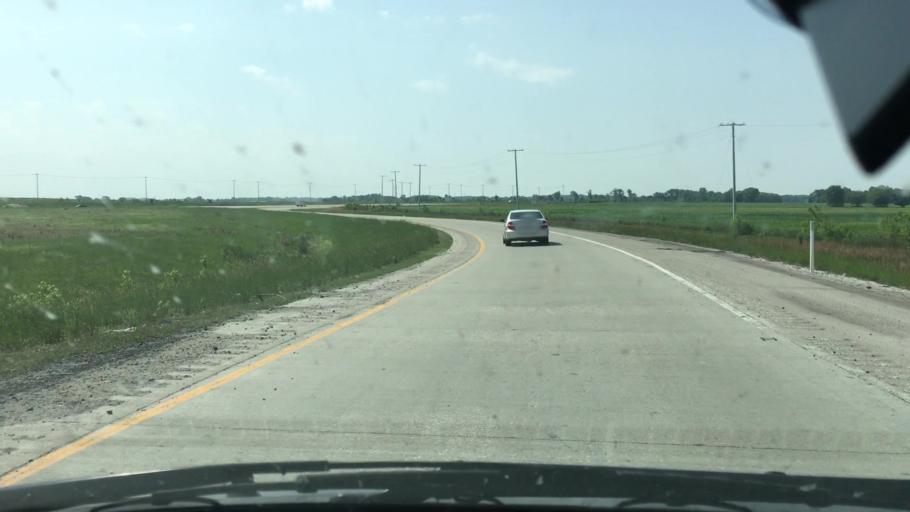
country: US
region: Indiana
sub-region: Daviess County
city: Washington
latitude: 38.6549
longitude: -87.1228
